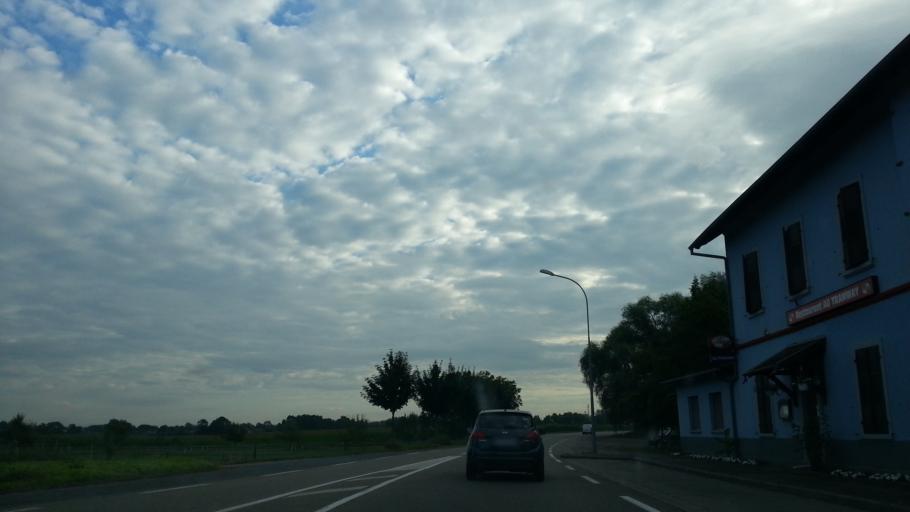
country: FR
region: Alsace
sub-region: Departement du Bas-Rhin
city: Gerstheim
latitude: 48.4078
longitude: 7.6988
